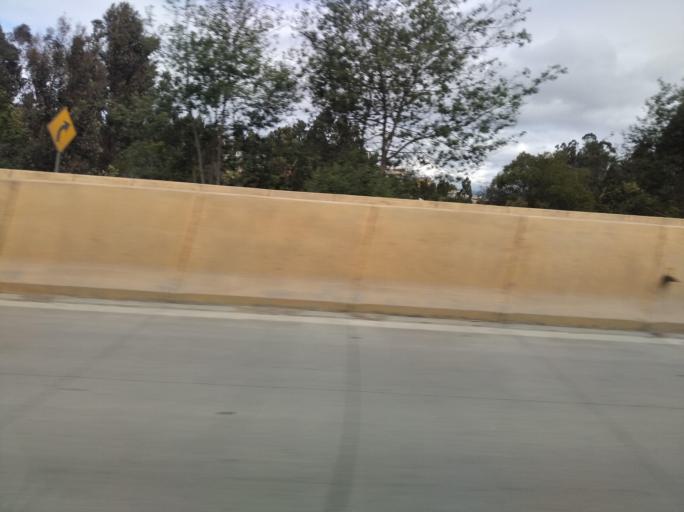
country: CL
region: Valparaiso
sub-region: Provincia de Valparaiso
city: Vina del Mar
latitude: -33.1065
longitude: -71.5631
